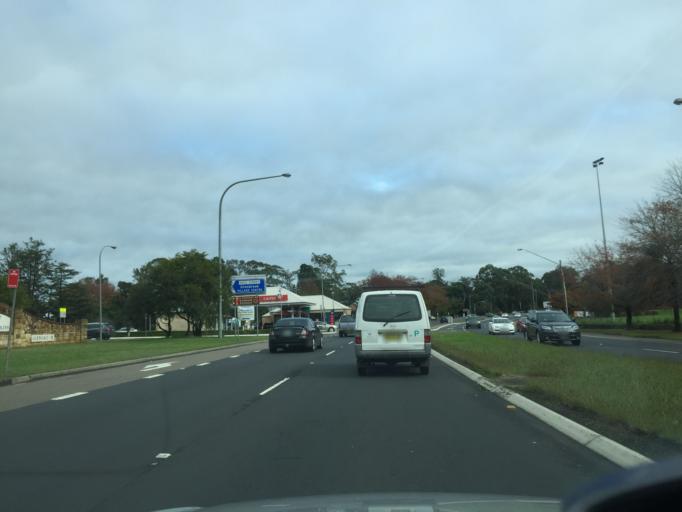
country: AU
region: New South Wales
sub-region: Blue Mountains Municipality
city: Glenbrook
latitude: -33.7651
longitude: 150.6226
